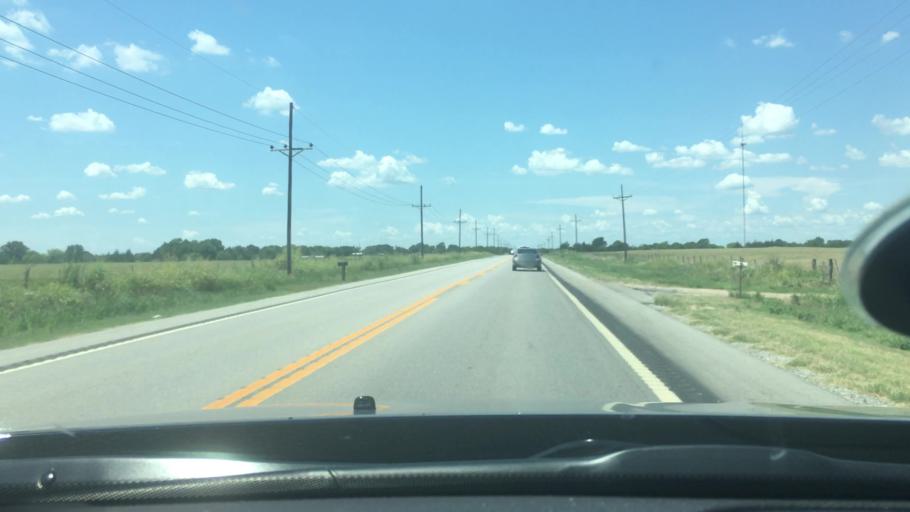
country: US
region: Oklahoma
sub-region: Bryan County
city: Durant
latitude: 33.9975
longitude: -96.2631
